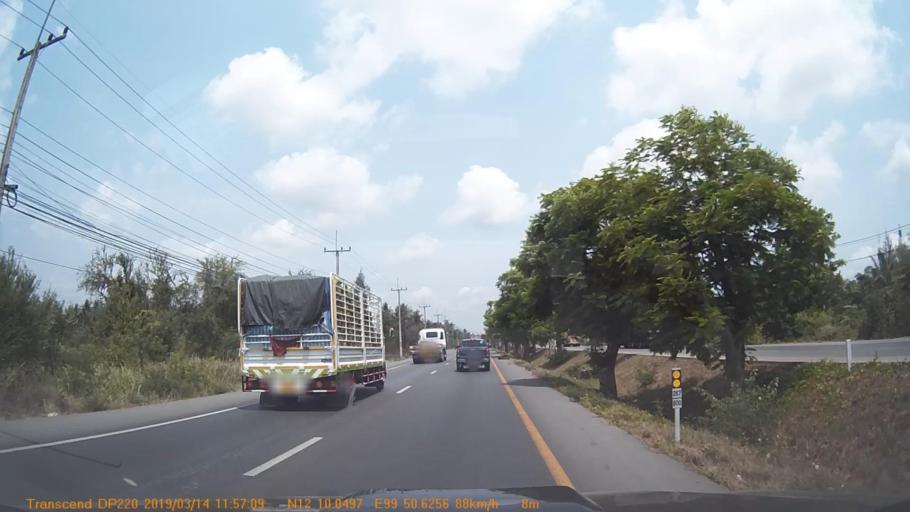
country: TH
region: Prachuap Khiri Khan
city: Kui Buri
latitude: 12.1680
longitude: 99.8438
